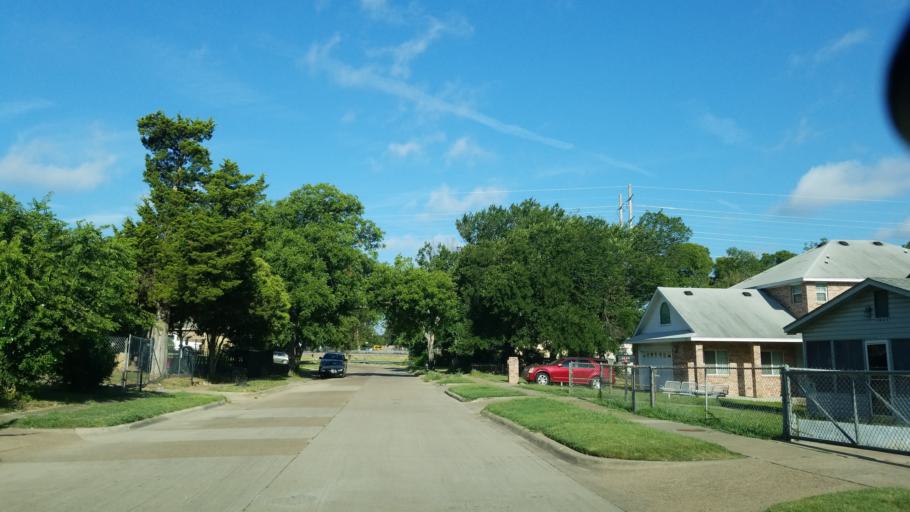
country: US
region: Texas
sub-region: Dallas County
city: Dallas
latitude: 32.7286
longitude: -96.8029
